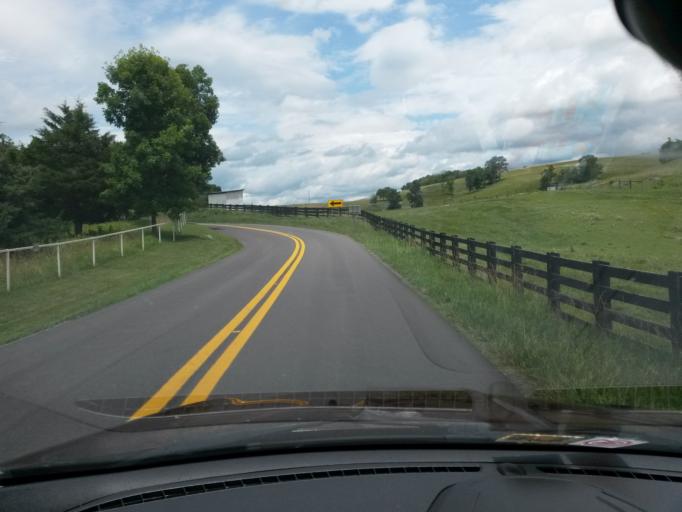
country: US
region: West Virginia
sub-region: Monroe County
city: Union
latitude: 37.5388
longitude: -80.5381
